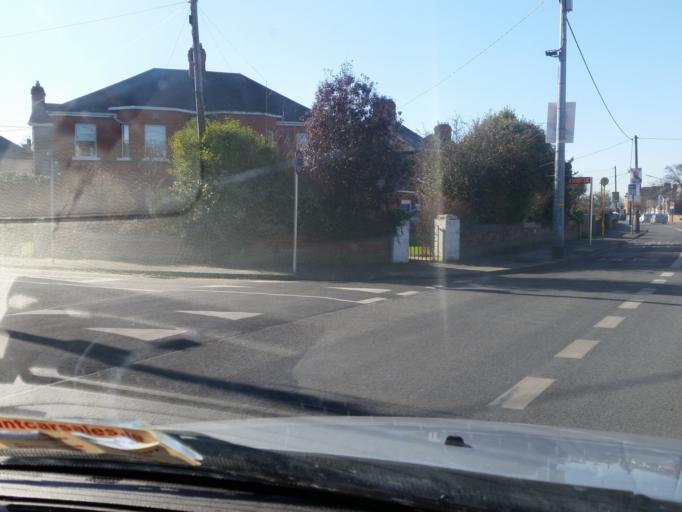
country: IE
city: Killester
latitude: 53.3749
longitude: -6.1975
